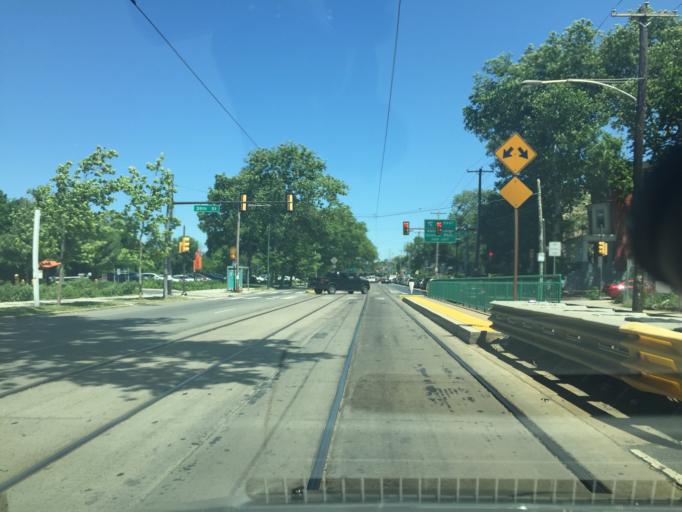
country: US
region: Pennsylvania
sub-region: Philadelphia County
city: Philadelphia
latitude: 39.9743
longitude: -75.2024
